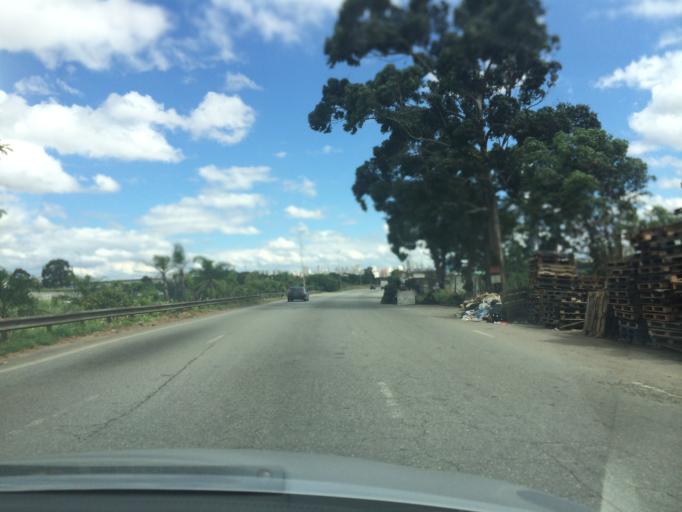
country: BR
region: Sao Paulo
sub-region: Guarulhos
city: Guarulhos
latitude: -23.5076
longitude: -46.5588
